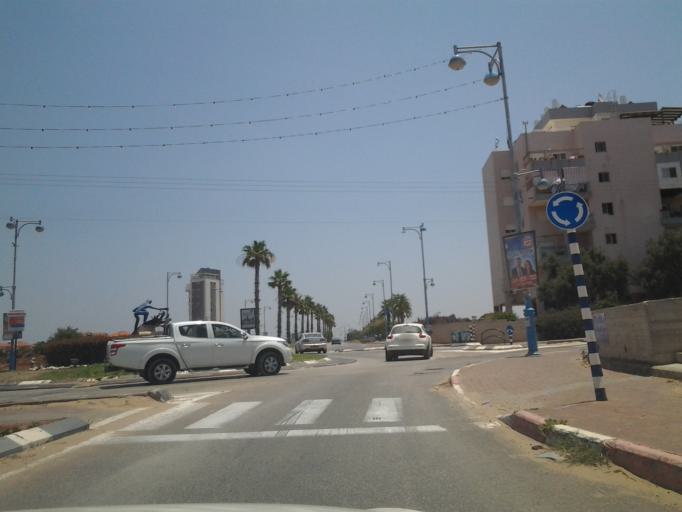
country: IL
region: Haifa
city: Hadera
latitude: 32.4440
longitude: 34.8864
